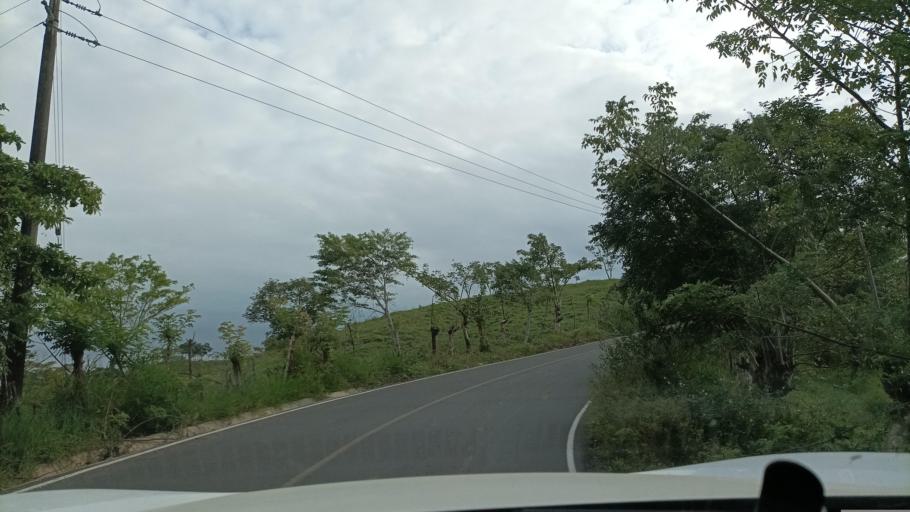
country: MX
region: Veracruz
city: Hidalgotitlan
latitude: 17.6901
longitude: -94.4603
